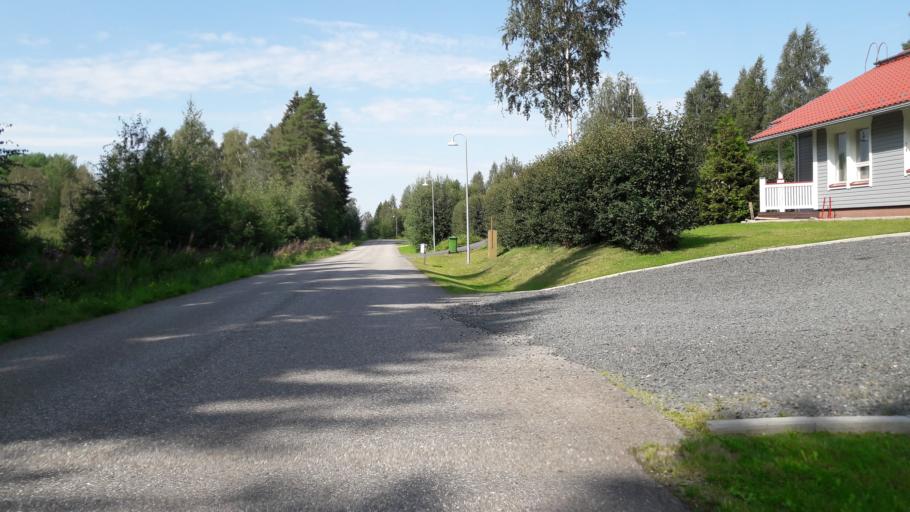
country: FI
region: North Karelia
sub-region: Joensuu
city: Joensuu
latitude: 62.5252
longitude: 29.8421
